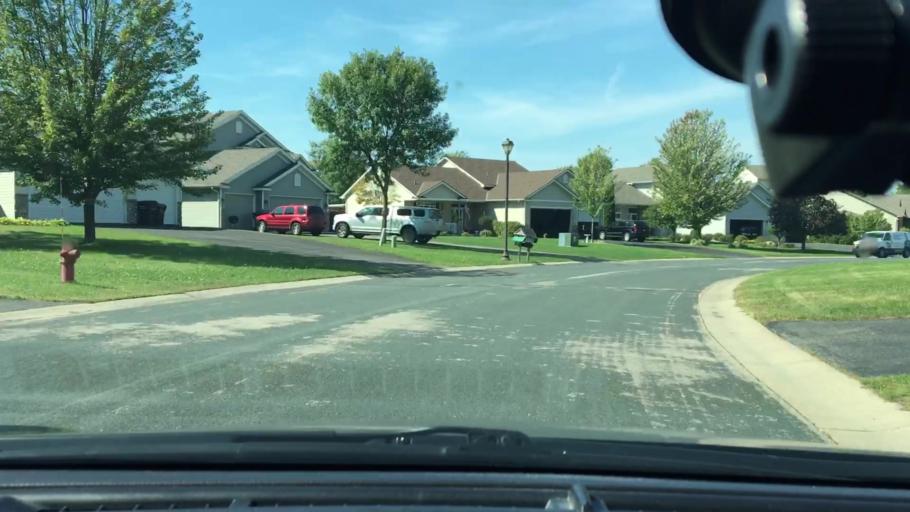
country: US
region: Minnesota
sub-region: Wright County
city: Hanover
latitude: 45.1628
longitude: -93.6766
